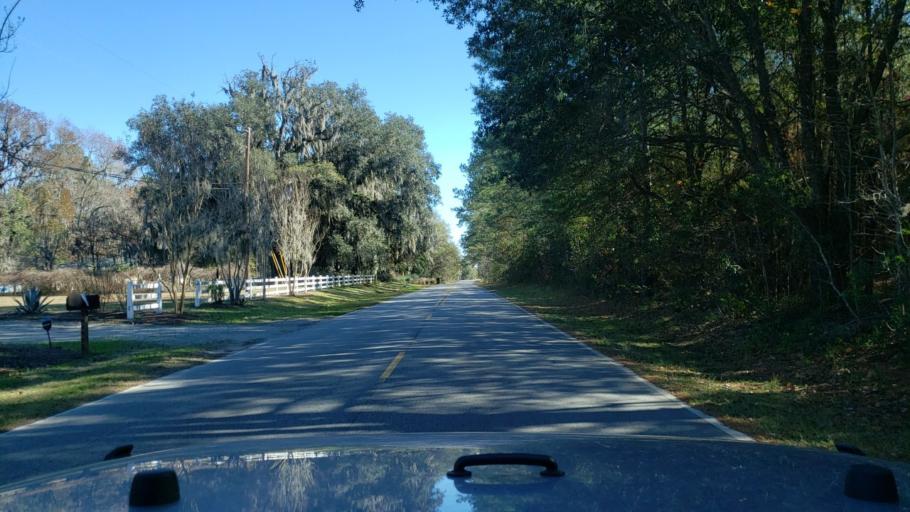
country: US
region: Georgia
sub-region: Chatham County
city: Georgetown
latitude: 32.0325
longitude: -81.1855
